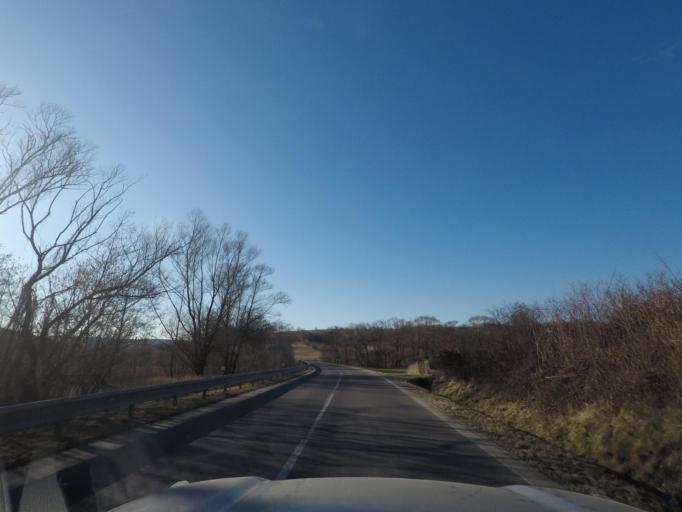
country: SK
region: Presovsky
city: Stropkov
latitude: 49.2608
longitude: 21.7473
